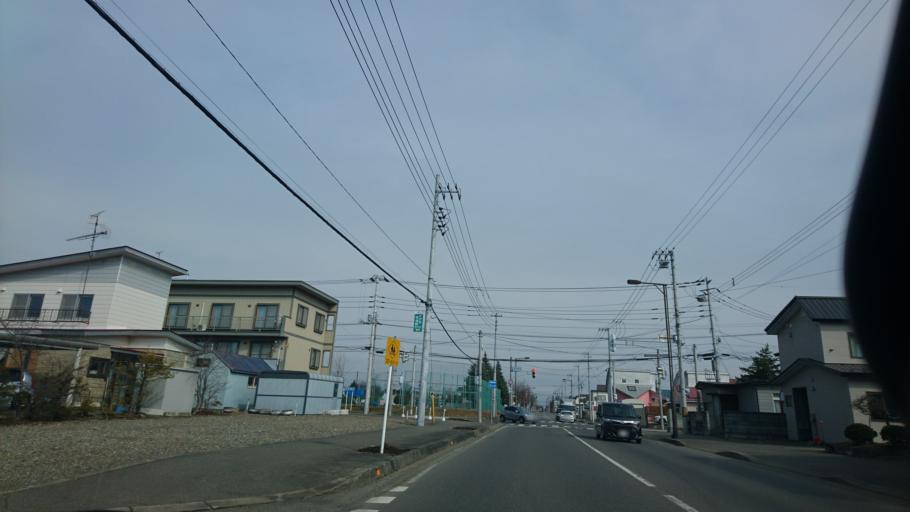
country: JP
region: Hokkaido
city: Otofuke
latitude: 42.9673
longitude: 143.2130
